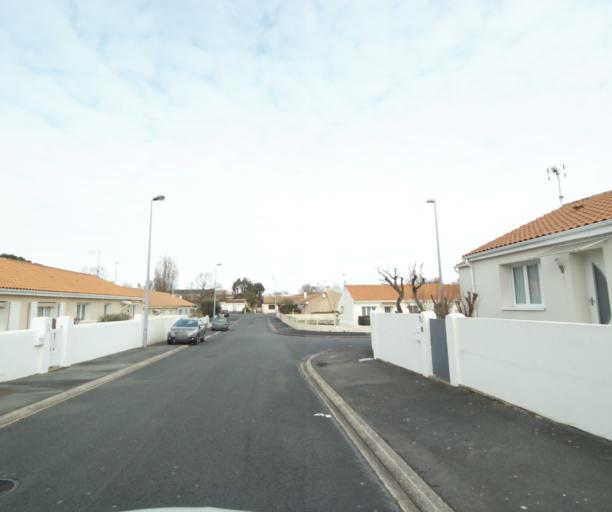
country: FR
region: Poitou-Charentes
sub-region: Departement de la Charente-Maritime
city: Lagord
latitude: 46.1810
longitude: -1.1580
